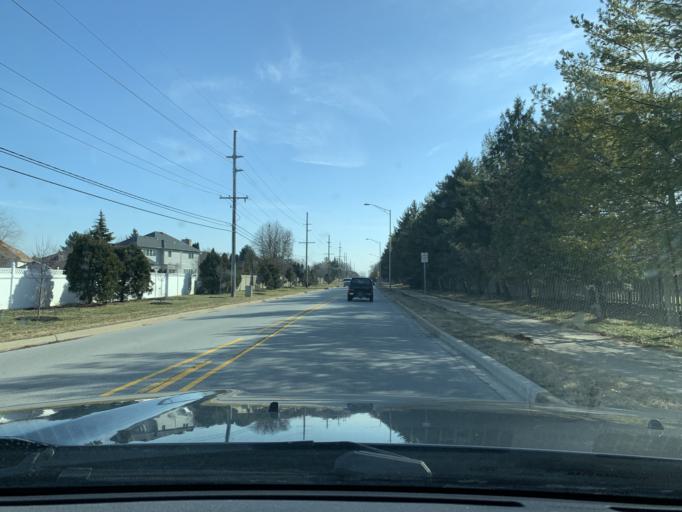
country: US
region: Indiana
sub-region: Lake County
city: Munster
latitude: 41.5295
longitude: -87.4904
